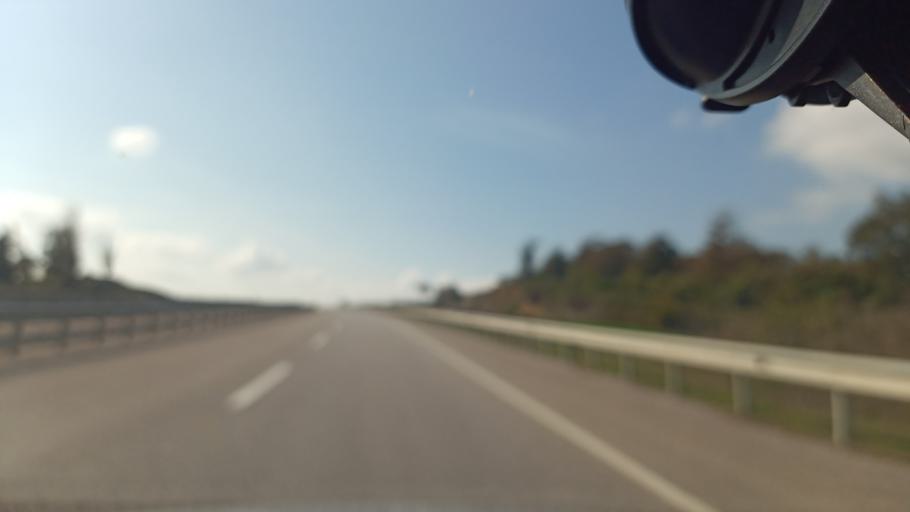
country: TR
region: Sakarya
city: Kaynarca
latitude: 41.0579
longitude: 30.3498
